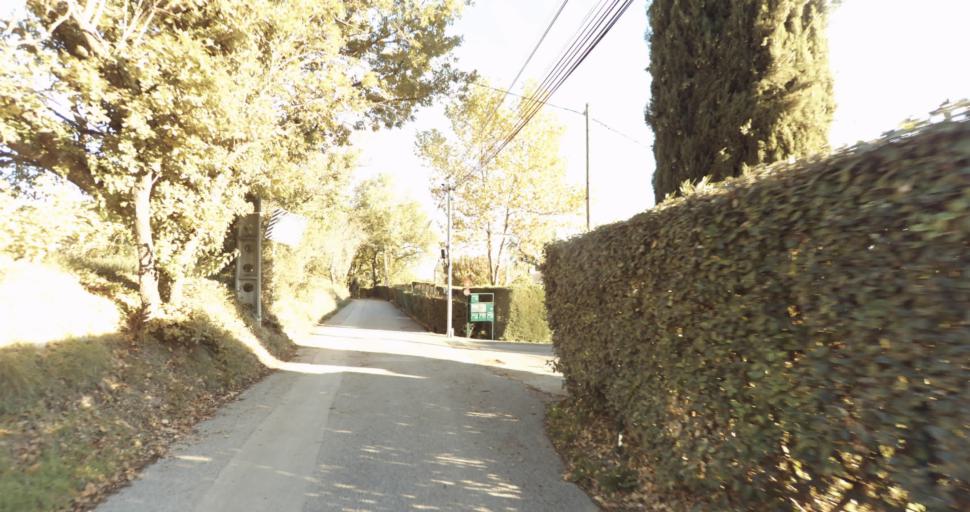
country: FR
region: Provence-Alpes-Cote d'Azur
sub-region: Departement des Bouches-du-Rhone
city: Venelles
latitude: 43.6067
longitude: 5.4817
